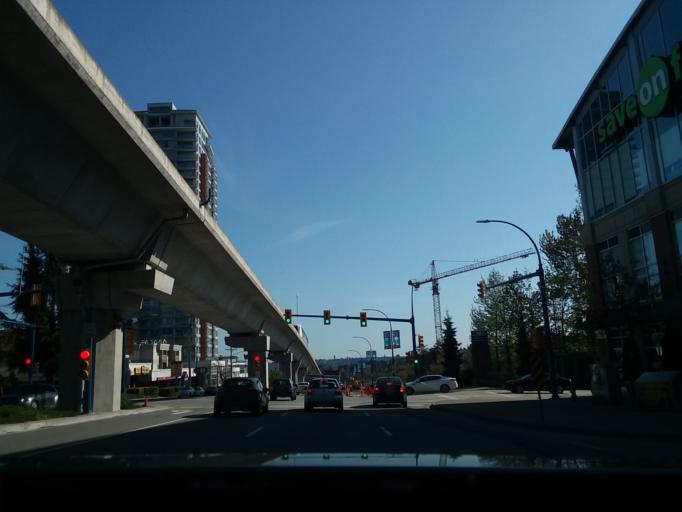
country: CA
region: British Columbia
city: New Westminster
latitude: 49.2524
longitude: -122.8931
